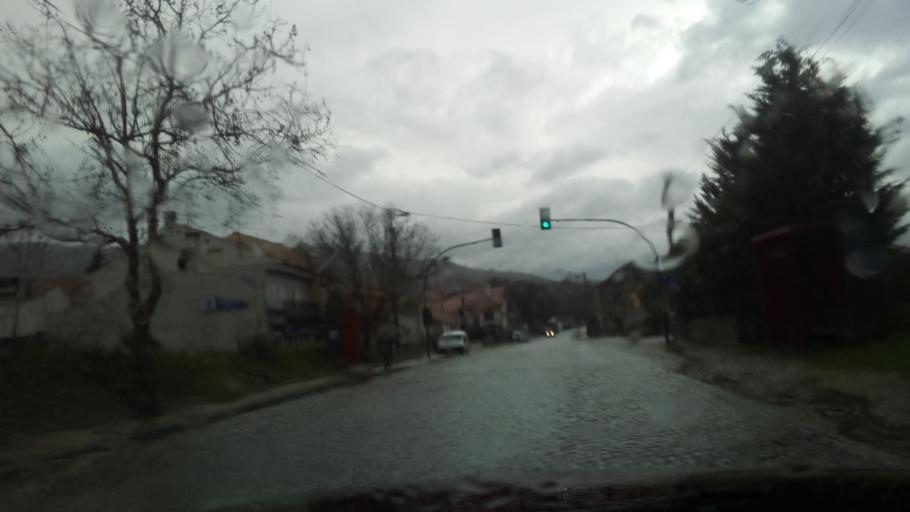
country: PT
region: Guarda
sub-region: Guarda
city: Guarda
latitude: 40.6027
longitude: -7.2954
